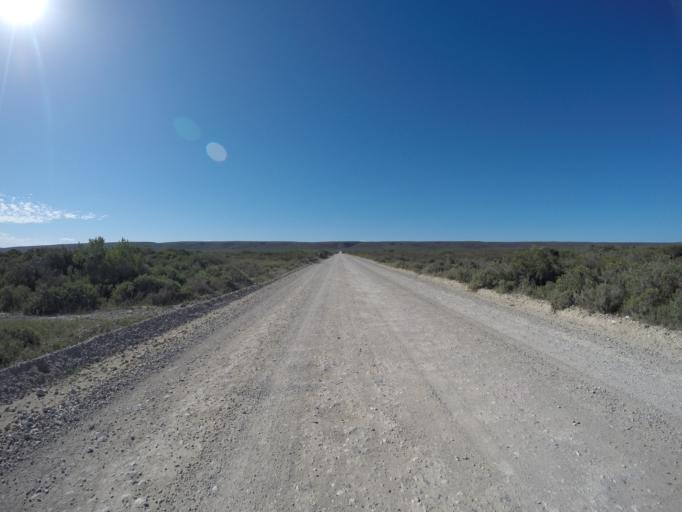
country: ZA
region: Western Cape
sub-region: Overberg District Municipality
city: Bredasdorp
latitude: -34.4468
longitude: 20.4223
